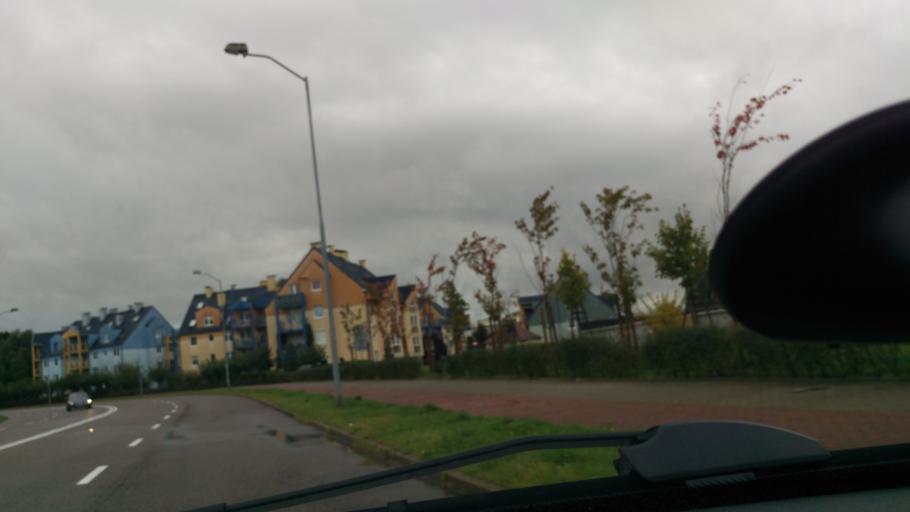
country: PL
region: West Pomeranian Voivodeship
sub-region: Szczecin
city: Szczecin
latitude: 53.3663
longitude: 14.6672
